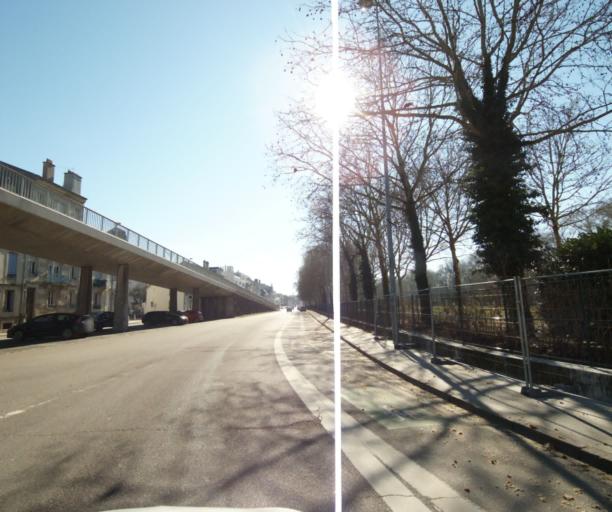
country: FR
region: Lorraine
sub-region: Departement de Meurthe-et-Moselle
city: Malzeville
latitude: 48.7005
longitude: 6.1863
